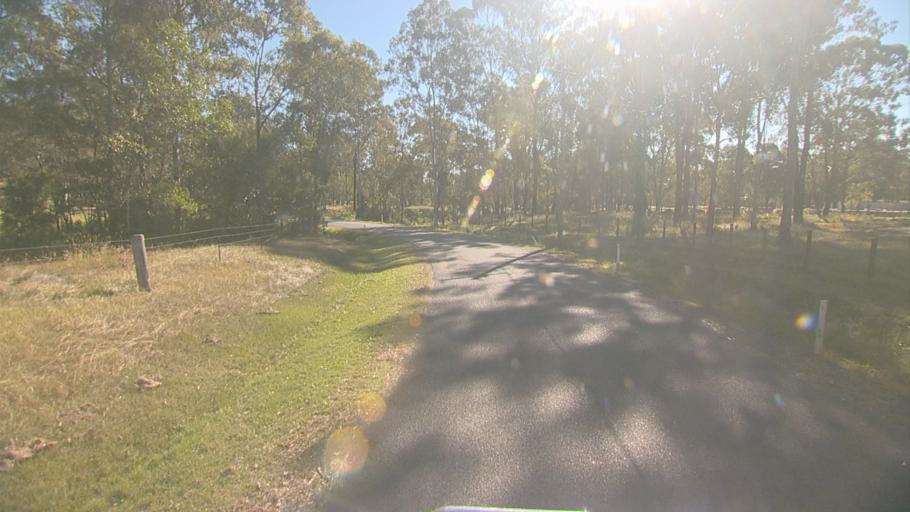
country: AU
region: Queensland
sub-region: Logan
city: Windaroo
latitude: -27.7615
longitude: 153.1492
